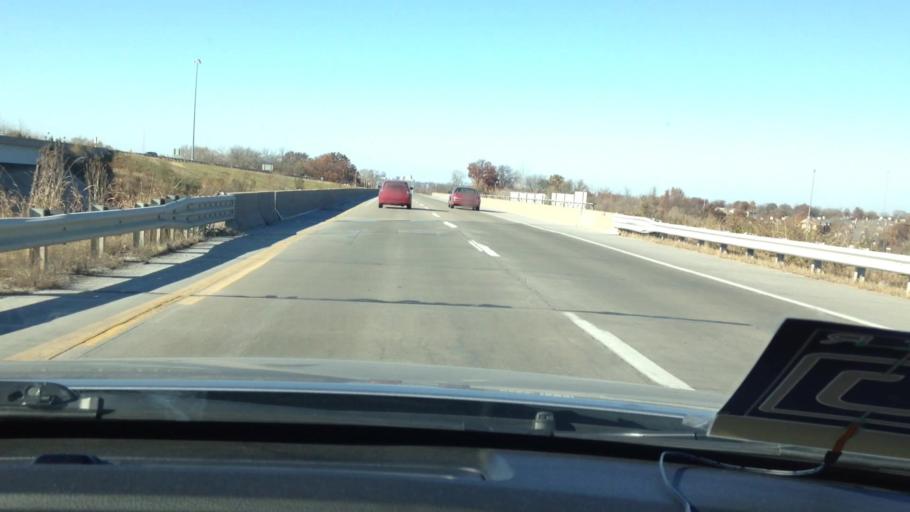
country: US
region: Missouri
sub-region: Jackson County
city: Raytown
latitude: 39.0205
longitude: -94.5000
